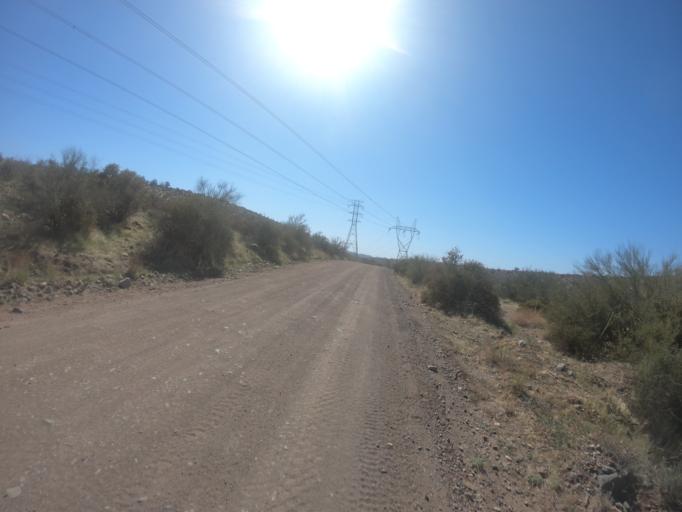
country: US
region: Arizona
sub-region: Pinal County
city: Superior
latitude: 33.2981
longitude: -111.1405
